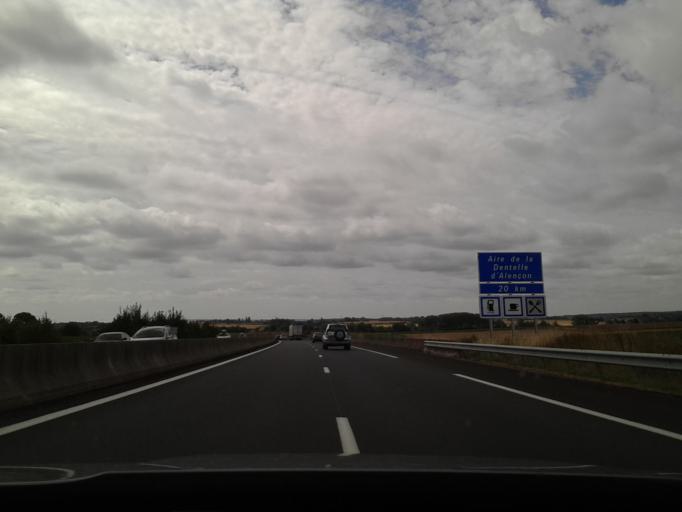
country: FR
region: Lower Normandy
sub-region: Departement de l'Orne
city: Sees
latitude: 48.6175
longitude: 0.1915
